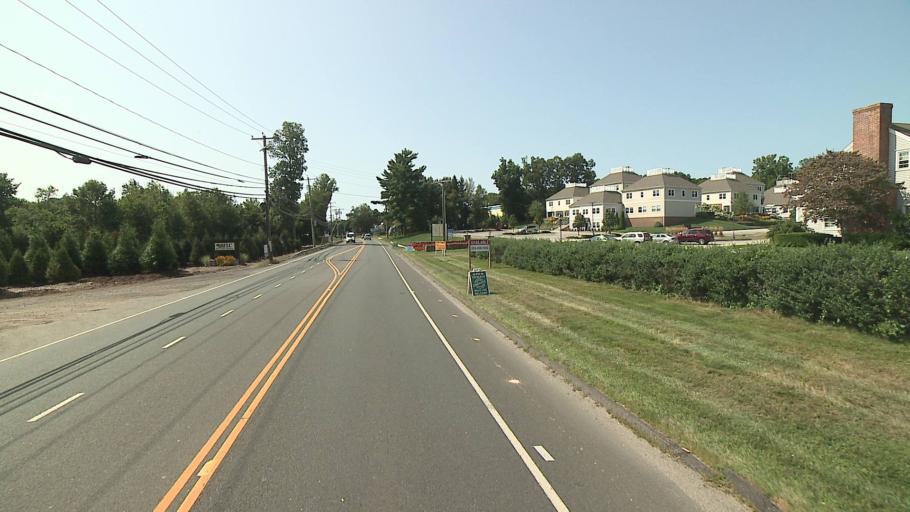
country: US
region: Connecticut
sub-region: Fairfield County
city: Newtown
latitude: 41.3423
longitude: -73.2614
